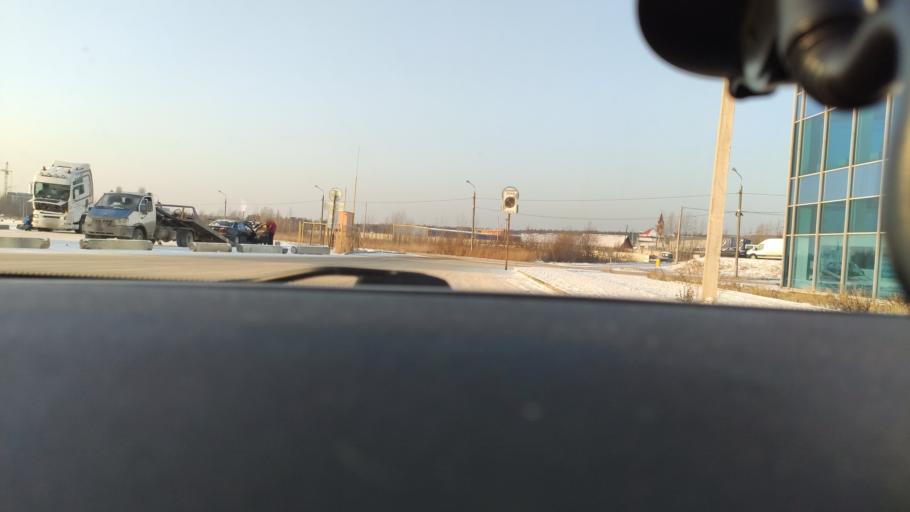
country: RU
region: Perm
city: Perm
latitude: 58.0347
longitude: 56.1962
